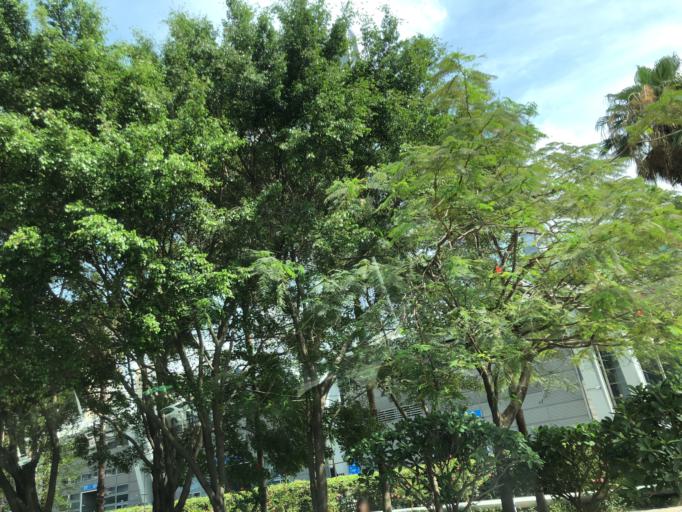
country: CN
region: Guangdong
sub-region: Shenzhen
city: Shenzhen
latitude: 22.5317
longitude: 114.0535
